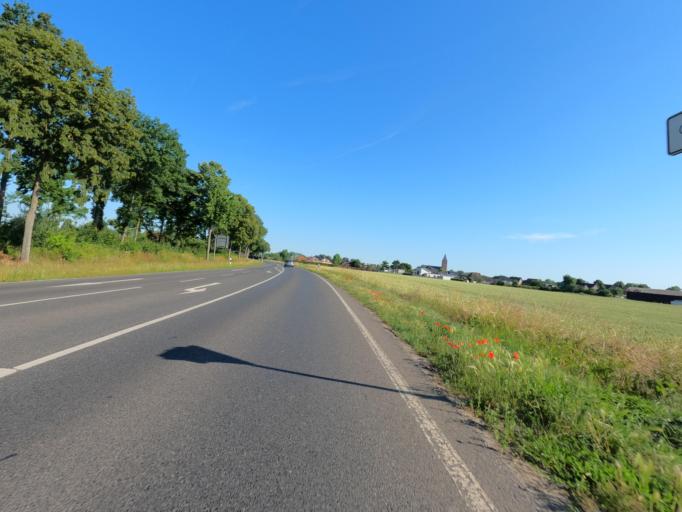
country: DE
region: North Rhine-Westphalia
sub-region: Regierungsbezirk Koln
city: Heinsberg
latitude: 51.0890
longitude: 6.1016
